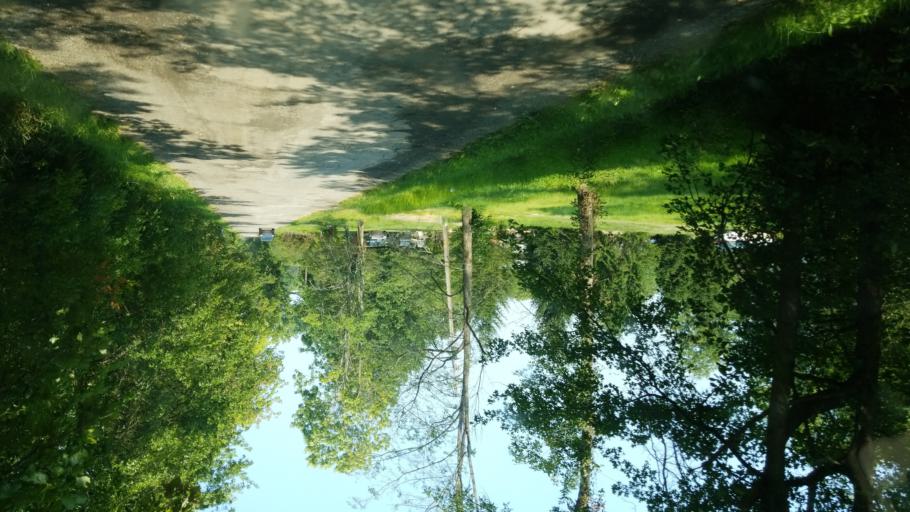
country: US
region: Ohio
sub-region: Ashtabula County
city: Orwell
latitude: 41.4908
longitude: -80.8982
